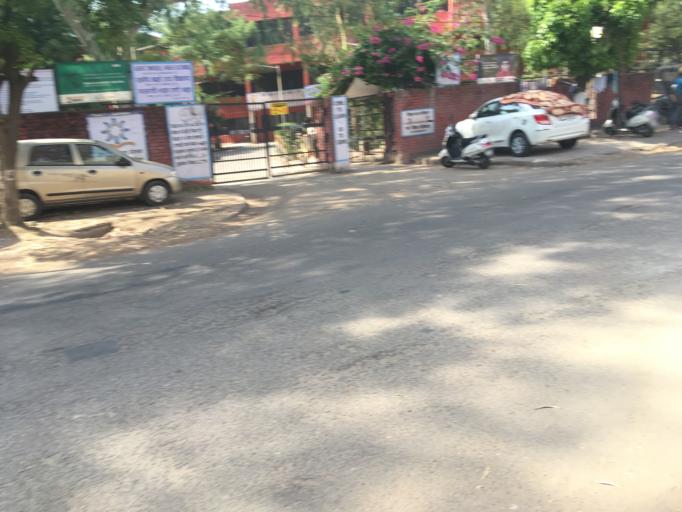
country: IN
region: Chandigarh
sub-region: Chandigarh
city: Chandigarh
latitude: 30.7093
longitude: 76.7938
